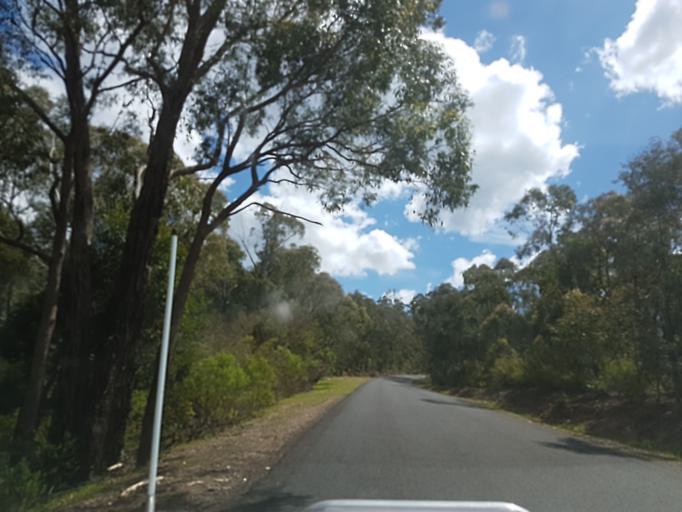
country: AU
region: Victoria
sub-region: East Gippsland
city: Bairnsdale
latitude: -37.4207
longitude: 147.2538
